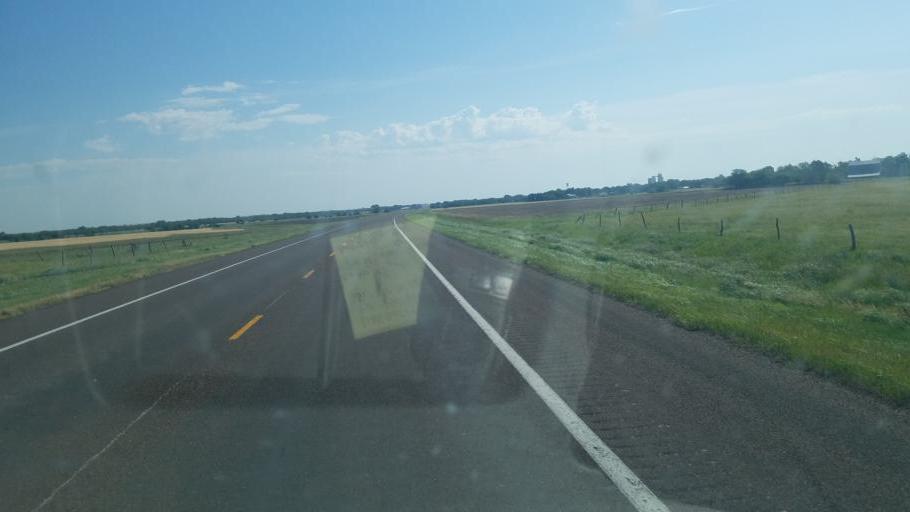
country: US
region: Kansas
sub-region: Ellsworth County
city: Ellsworth
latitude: 38.5809
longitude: -98.4306
